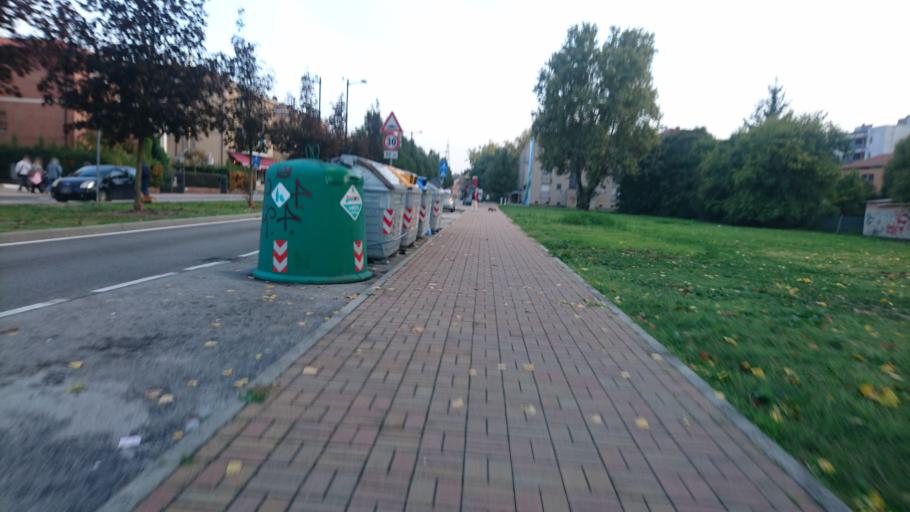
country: IT
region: Emilia-Romagna
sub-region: Provincia di Ferrara
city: Ferrara
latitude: 44.8626
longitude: 11.6068
